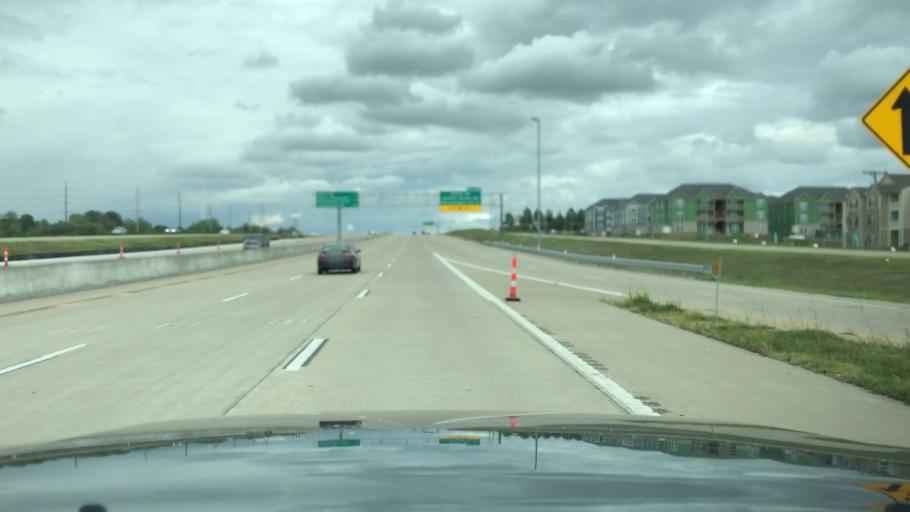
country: US
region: Missouri
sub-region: Saint Charles County
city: Cottleville
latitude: 38.7385
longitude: -90.6292
